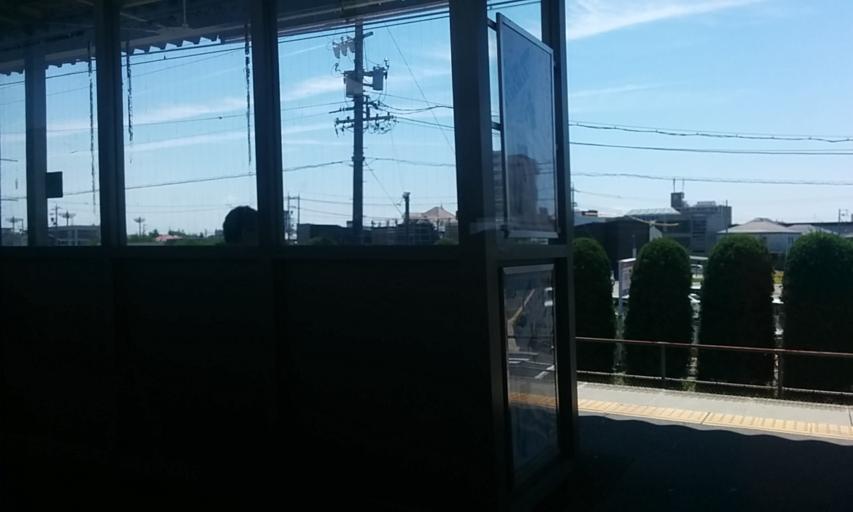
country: JP
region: Gifu
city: Gifu-shi
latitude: 35.4044
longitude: 136.7239
